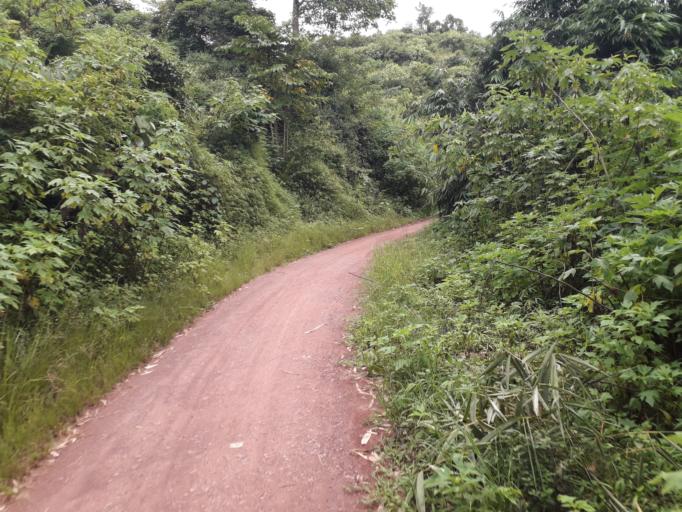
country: CN
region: Yunnan
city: Menglie
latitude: 22.2454
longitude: 101.6096
